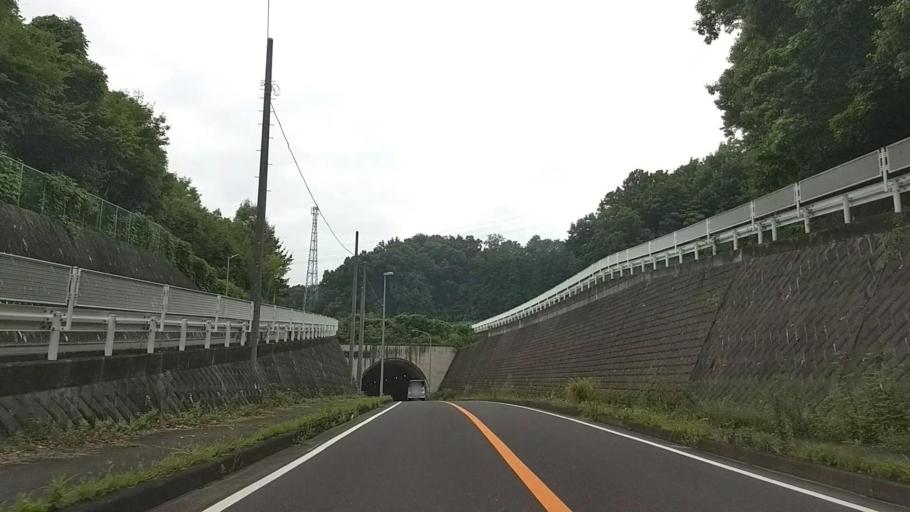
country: JP
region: Kanagawa
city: Hadano
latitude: 35.3391
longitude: 139.2278
